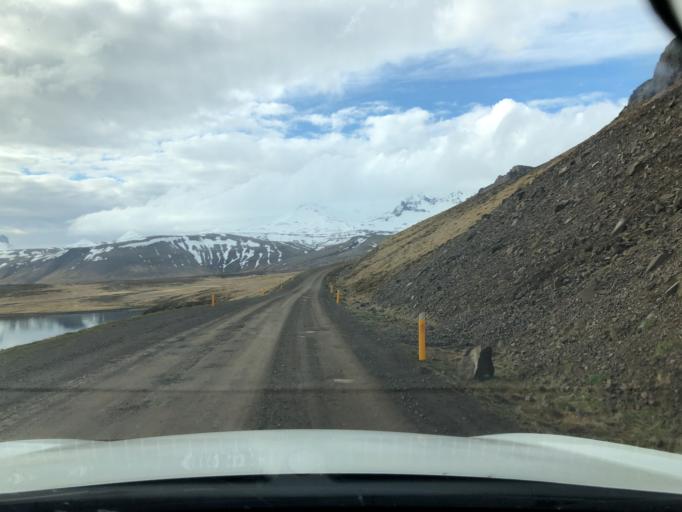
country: IS
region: West
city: Stykkisholmur
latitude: 64.9835
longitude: -22.6114
